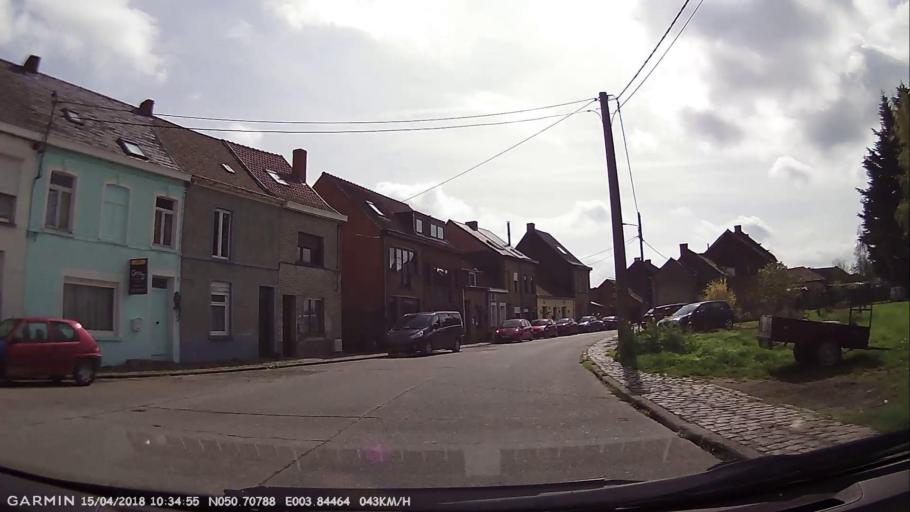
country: BE
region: Wallonia
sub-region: Province du Hainaut
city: Lessines
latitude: 50.7078
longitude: 3.8449
